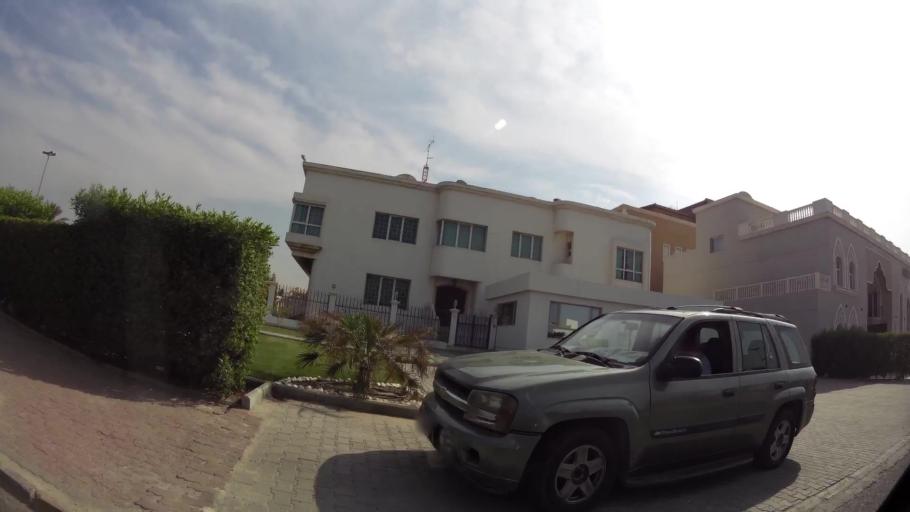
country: KW
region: Al Asimah
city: Ash Shamiyah
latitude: 29.3249
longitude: 47.9629
